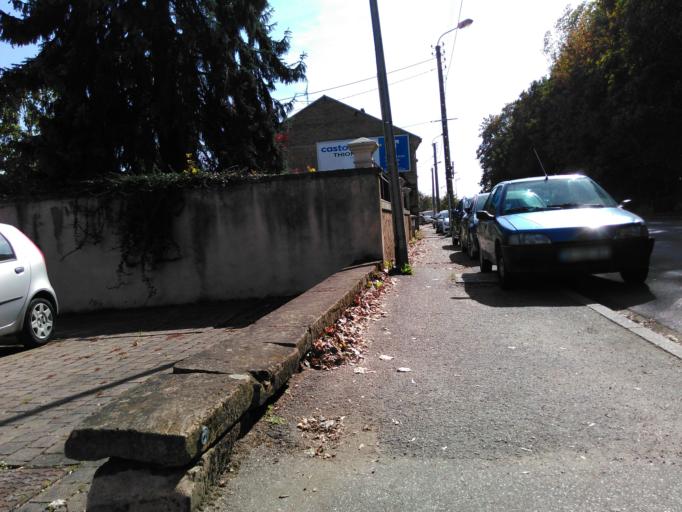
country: FR
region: Lorraine
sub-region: Departement de la Moselle
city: Thionville
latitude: 49.3749
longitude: 6.1694
